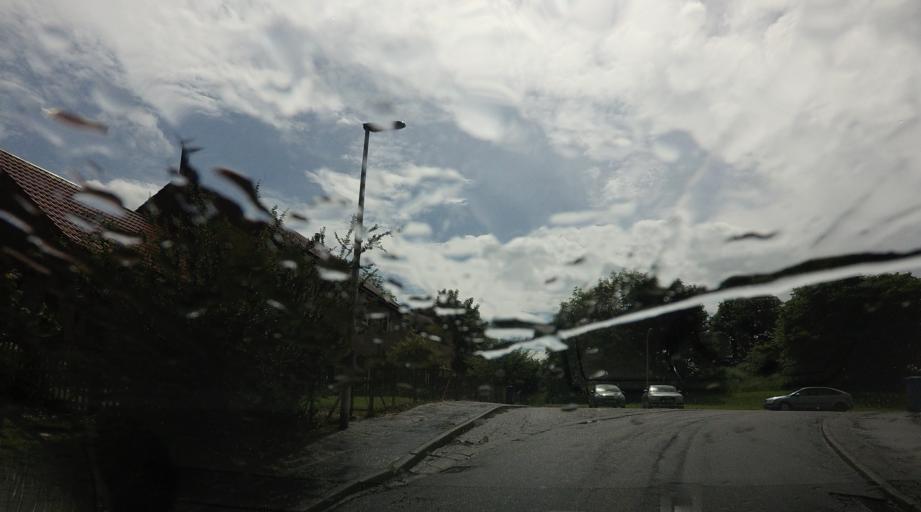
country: GB
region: Scotland
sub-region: Fife
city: Ballingry
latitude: 56.1609
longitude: -3.3316
